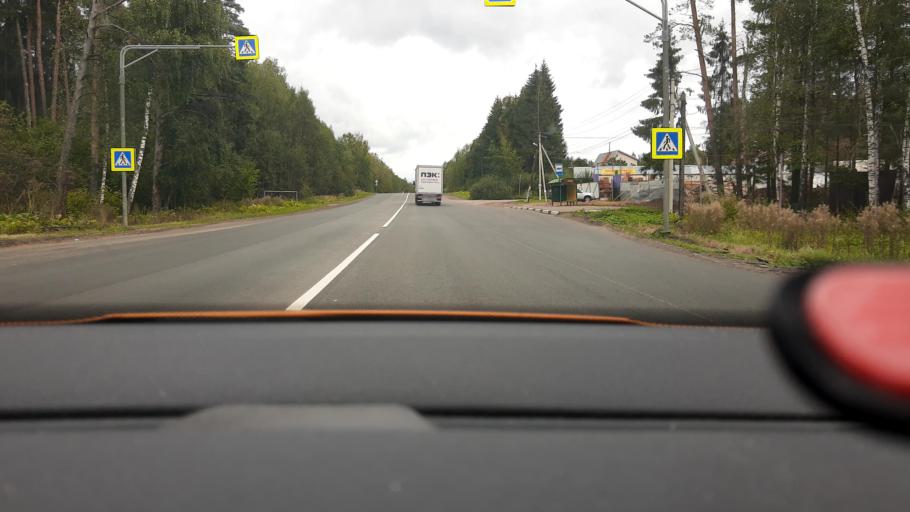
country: RU
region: Moskovskaya
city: Lesnoy
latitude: 56.0575
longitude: 38.0045
